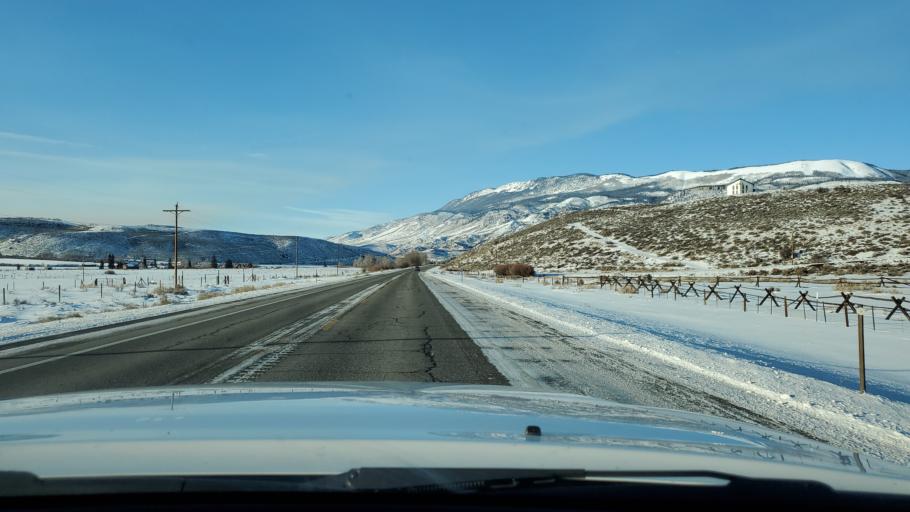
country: US
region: Colorado
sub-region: Summit County
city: Silverthorne
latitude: 39.7746
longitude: -106.1518
